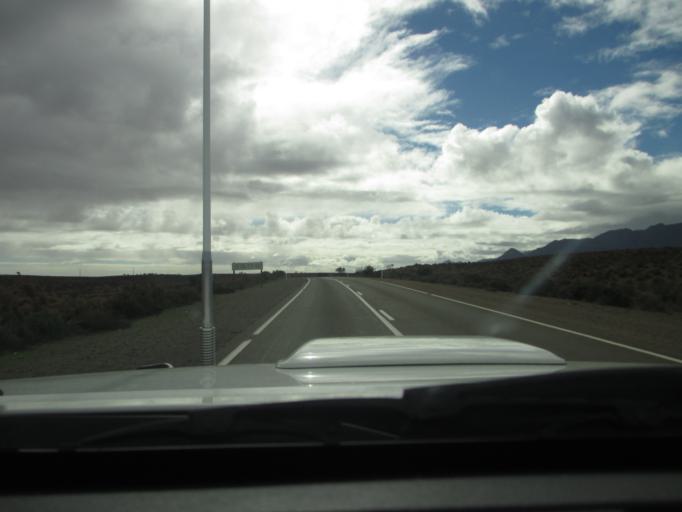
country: AU
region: South Australia
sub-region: Flinders Ranges
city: Quorn
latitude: -31.5654
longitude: 138.4277
